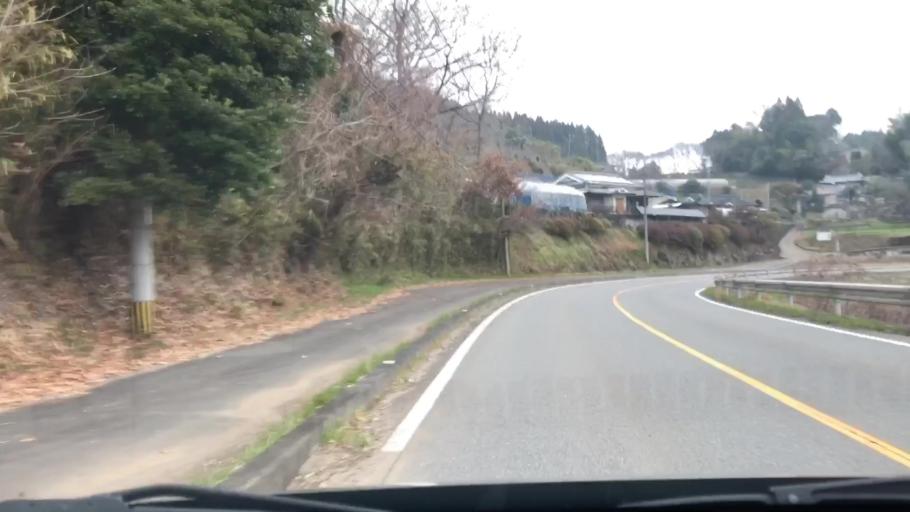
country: JP
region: Oita
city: Usuki
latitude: 33.0101
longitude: 131.6383
